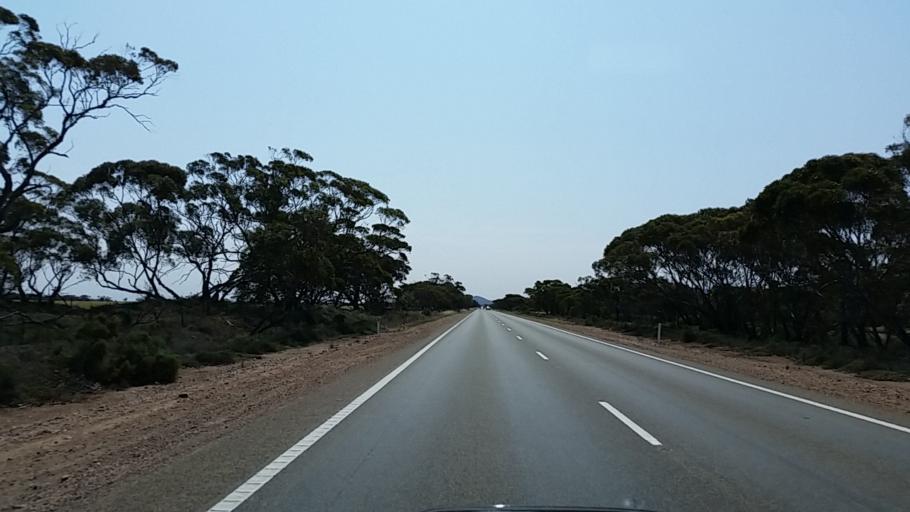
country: AU
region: South Australia
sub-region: Port Pirie City and Dists
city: Port Pirie
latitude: -32.9392
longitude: 137.9824
